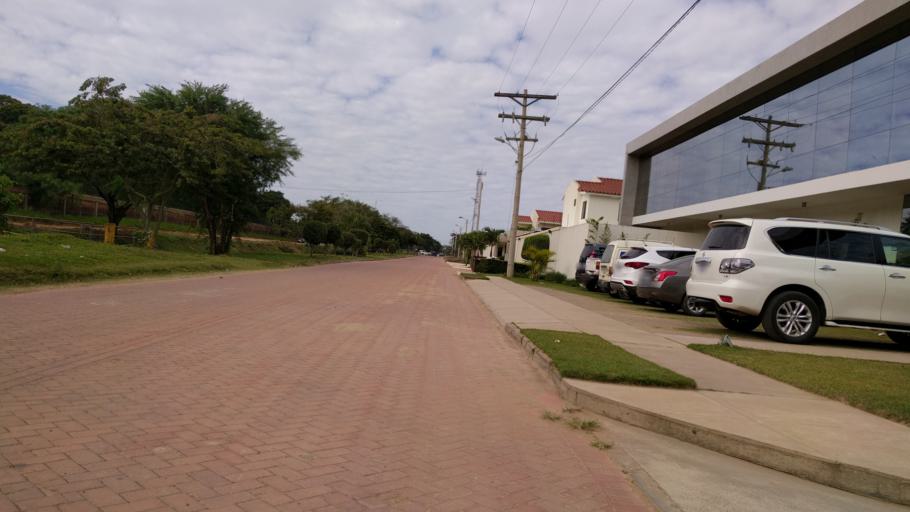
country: BO
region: Santa Cruz
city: Santa Cruz de la Sierra
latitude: -17.8116
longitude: -63.2321
